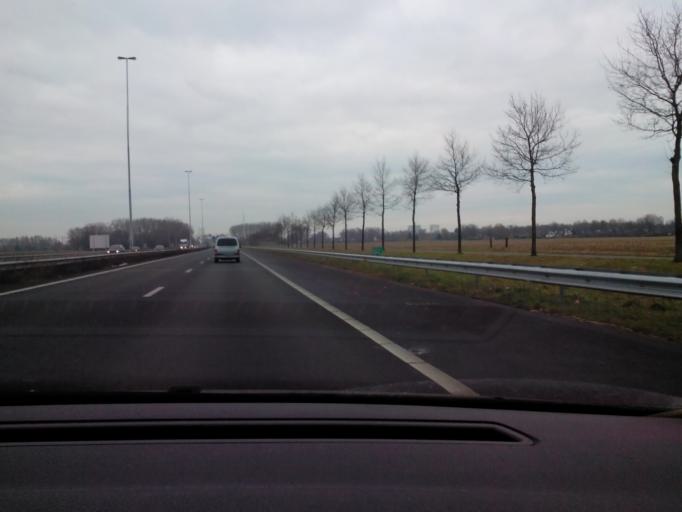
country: NL
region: South Holland
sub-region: Gemeente Gorinchem
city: Gorinchem
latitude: 51.8151
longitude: 4.9379
